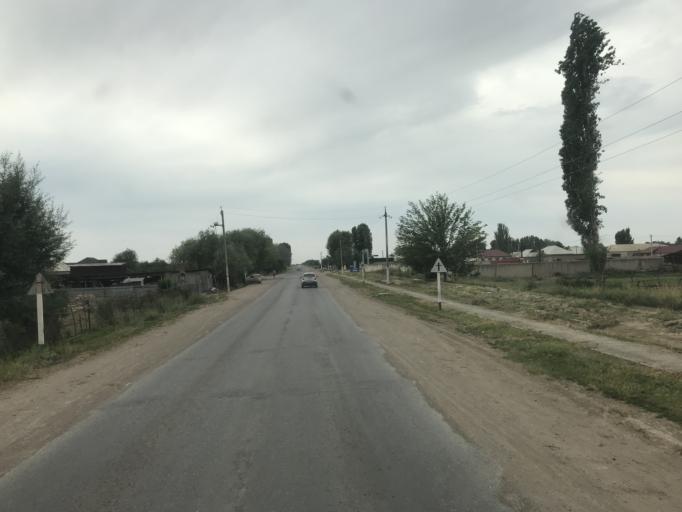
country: KZ
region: Ongtustik Qazaqstan
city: Asykata
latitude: 40.9049
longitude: 68.3550
